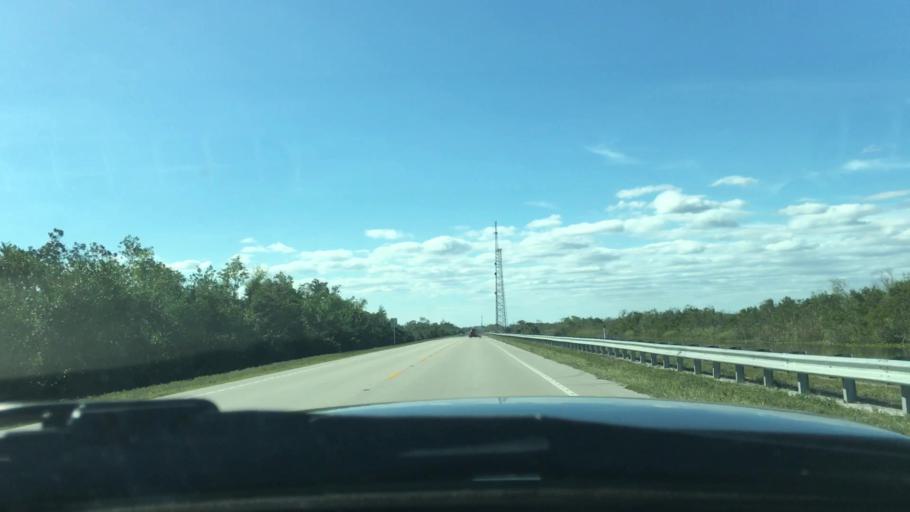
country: US
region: Florida
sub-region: Miami-Dade County
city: Kendall West
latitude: 25.7616
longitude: -80.8115
